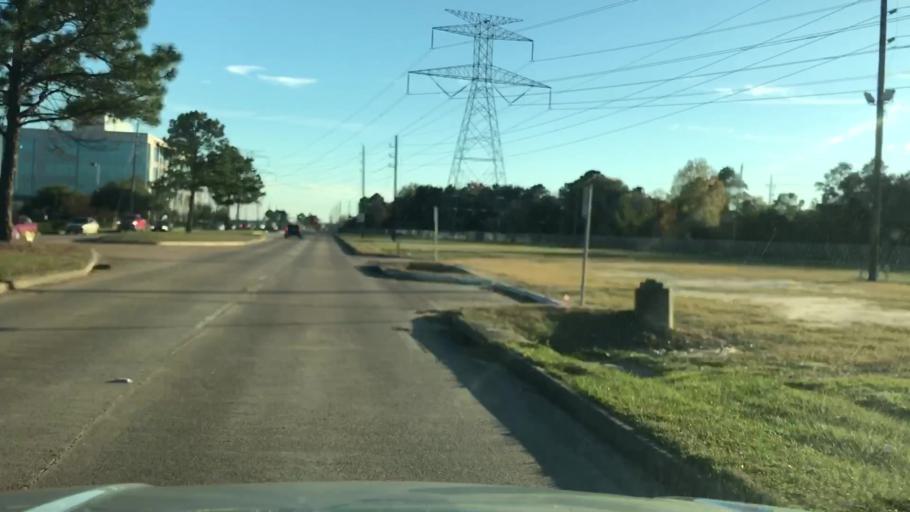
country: US
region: Texas
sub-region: Fort Bend County
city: Cinco Ranch
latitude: 29.7982
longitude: -95.7521
